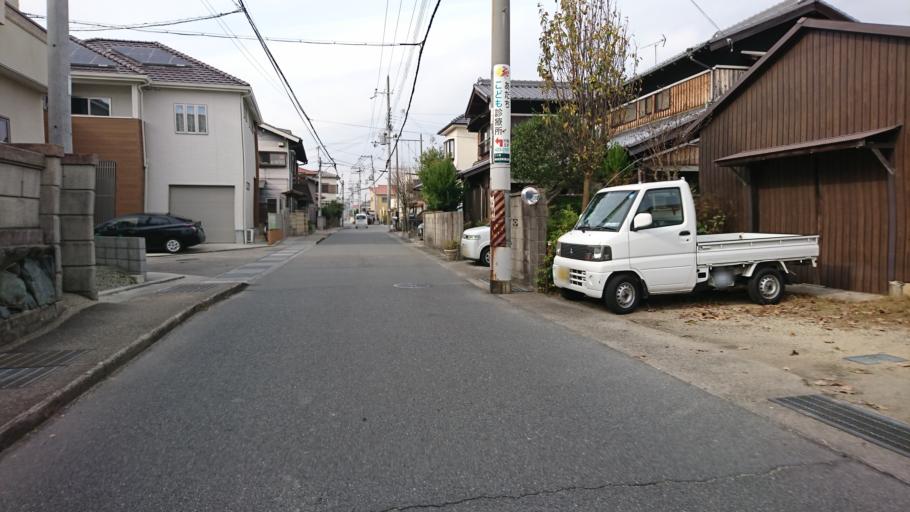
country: JP
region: Hyogo
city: Kakogawacho-honmachi
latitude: 34.7671
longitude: 134.8546
